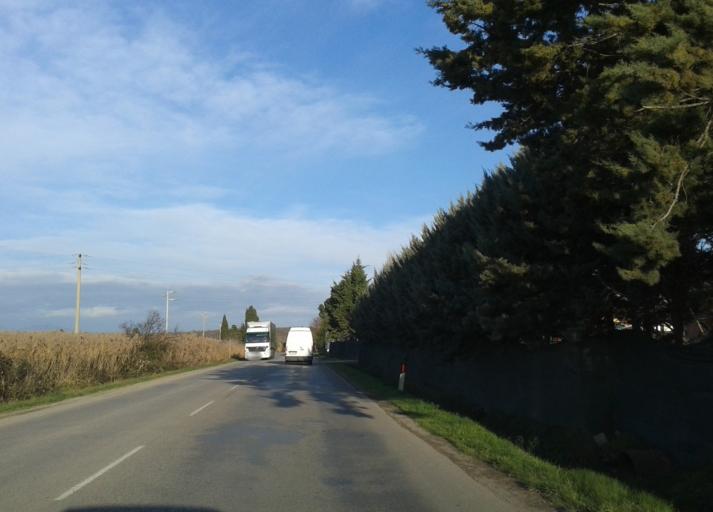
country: IT
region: Tuscany
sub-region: Provincia di Livorno
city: Livorno
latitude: 43.5709
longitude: 10.3671
